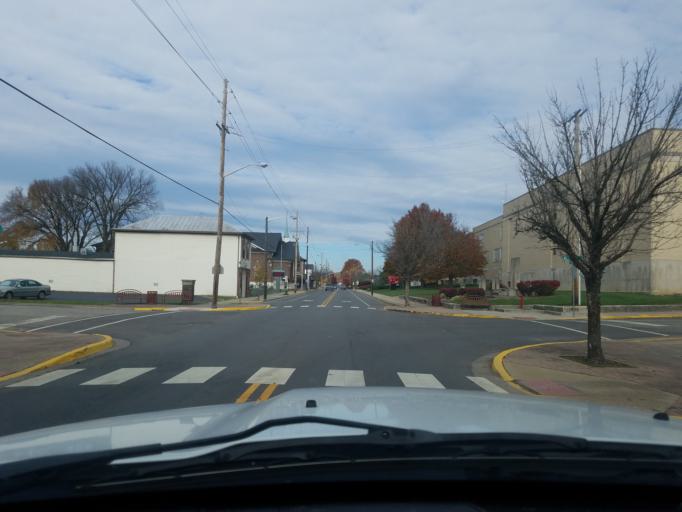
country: US
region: Indiana
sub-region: Floyd County
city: New Albany
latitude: 38.2968
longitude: -85.8108
